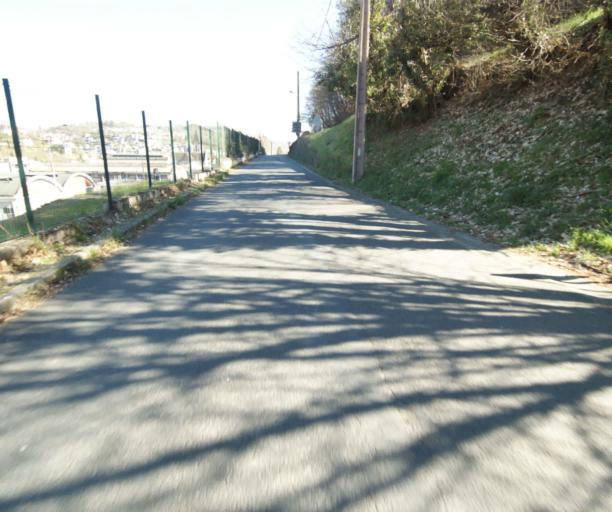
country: FR
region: Limousin
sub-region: Departement de la Correze
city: Tulle
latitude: 45.2613
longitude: 1.7461
